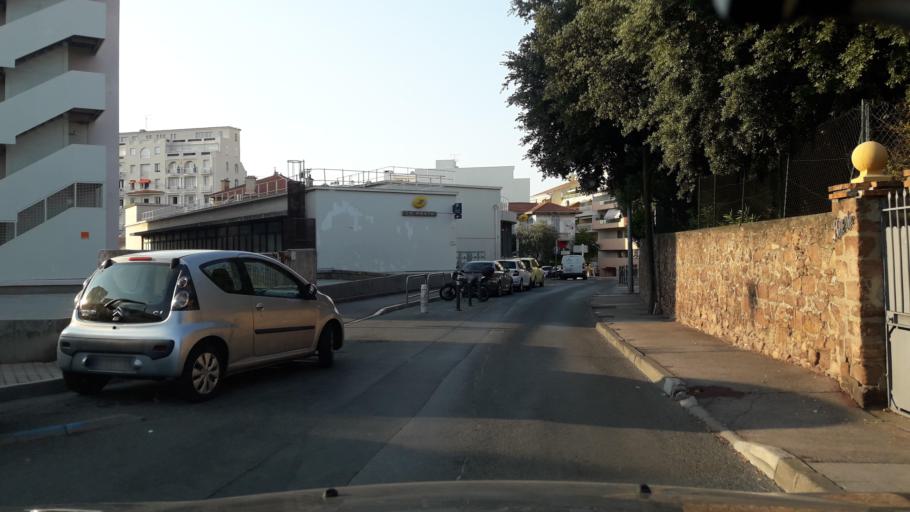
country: FR
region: Provence-Alpes-Cote d'Azur
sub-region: Departement du Var
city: Saint-Raphael
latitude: 43.4224
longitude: 6.7710
